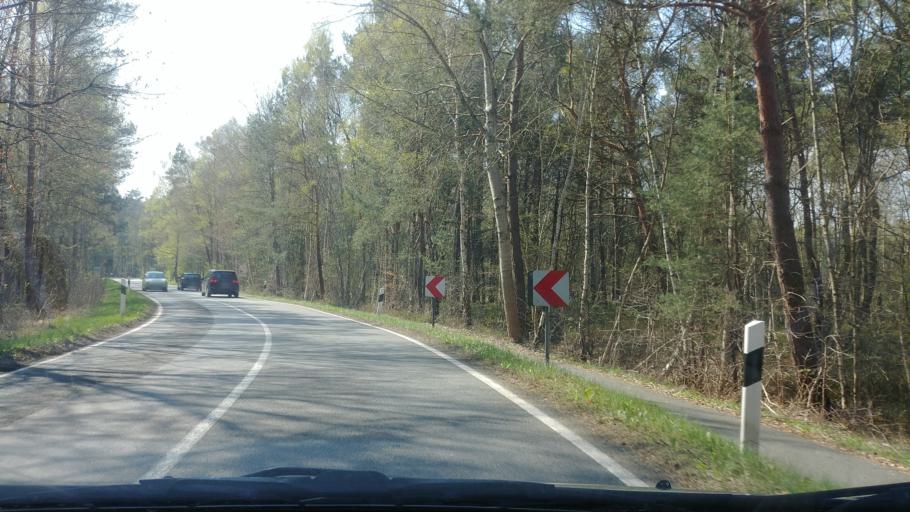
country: DE
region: Lower Saxony
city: Hagenburg
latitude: 52.5004
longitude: 9.3503
